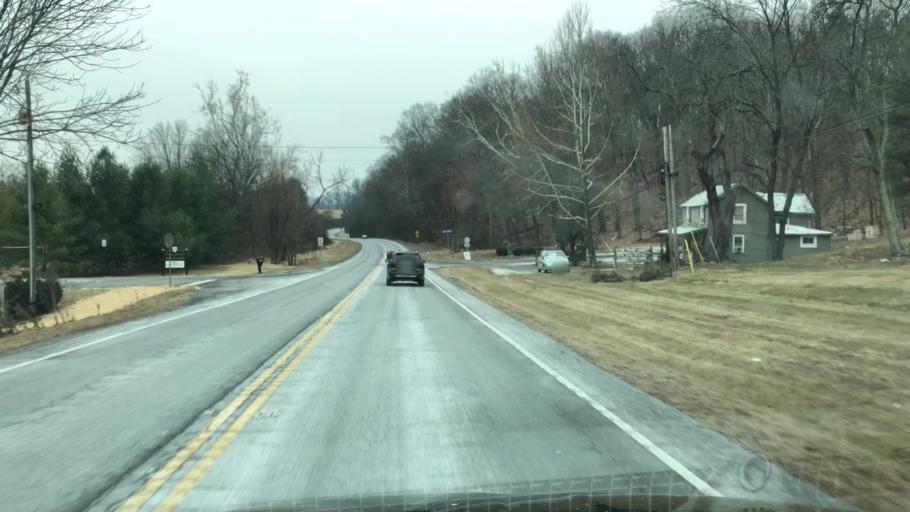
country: US
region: Virginia
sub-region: Loudoun County
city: Leesburg
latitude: 39.0556
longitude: -77.6176
